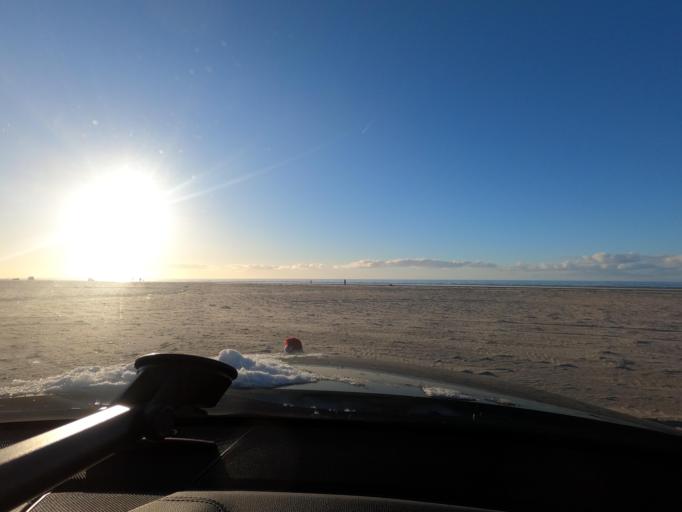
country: DE
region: Schleswig-Holstein
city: List
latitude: 55.1584
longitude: 8.4784
